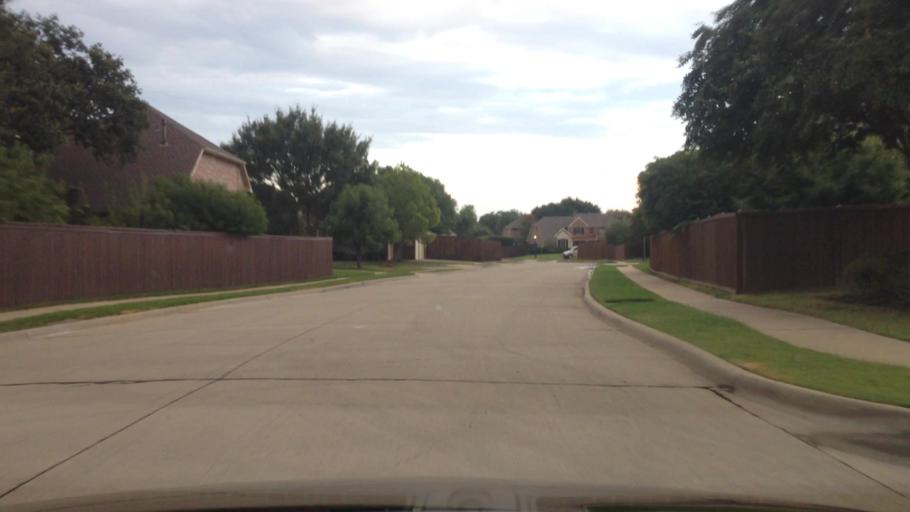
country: US
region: Texas
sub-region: Denton County
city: Flower Mound
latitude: 33.0050
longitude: -97.0432
